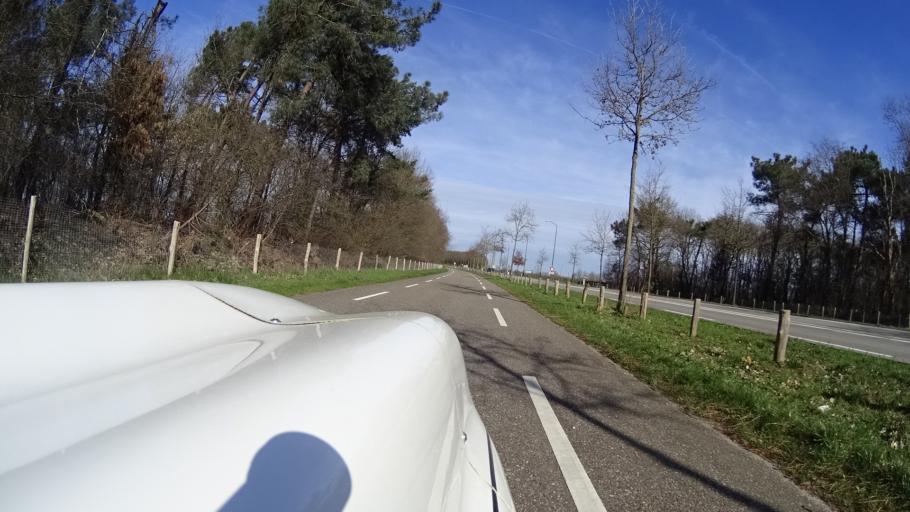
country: NL
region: North Brabant
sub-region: Gemeente Uden
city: Odiliapeel
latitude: 51.6753
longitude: 5.7304
